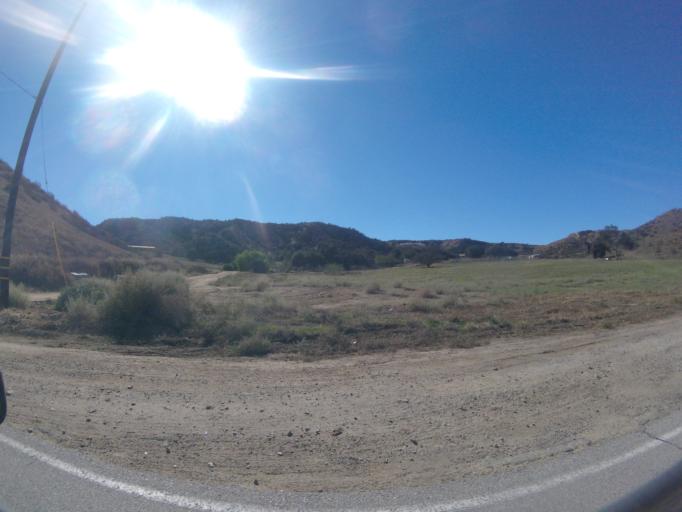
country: US
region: California
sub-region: Riverside County
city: Calimesa
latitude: 34.0076
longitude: -117.1079
